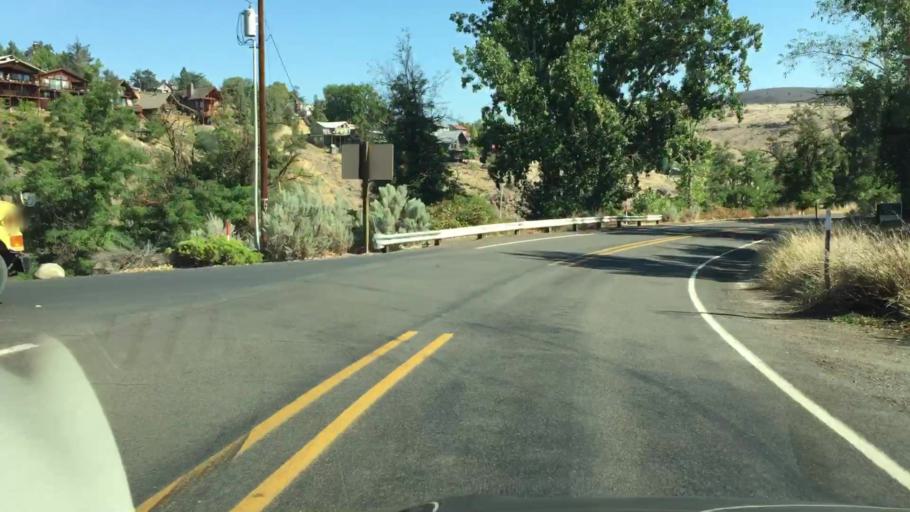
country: US
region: Oregon
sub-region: Wasco County
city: The Dalles
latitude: 45.1702
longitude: -121.0800
